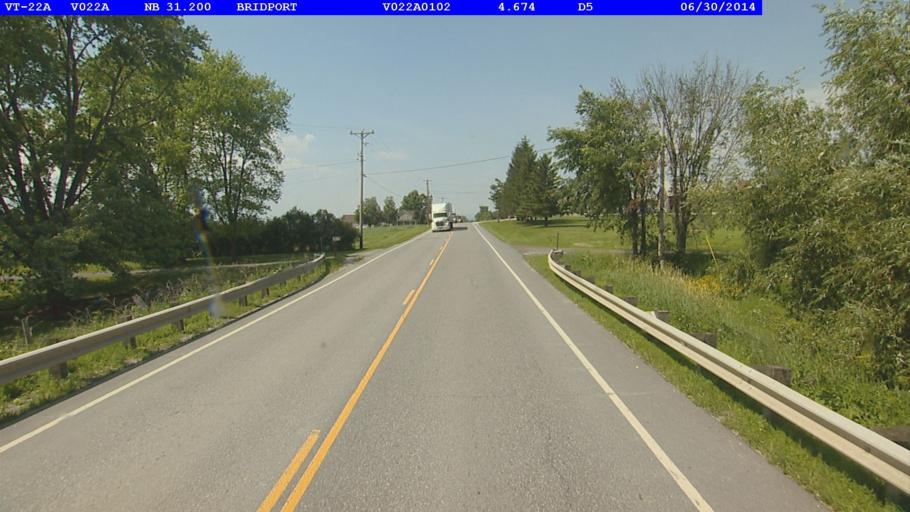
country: US
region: Vermont
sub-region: Addison County
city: Middlebury (village)
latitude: 44.0070
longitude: -73.3086
